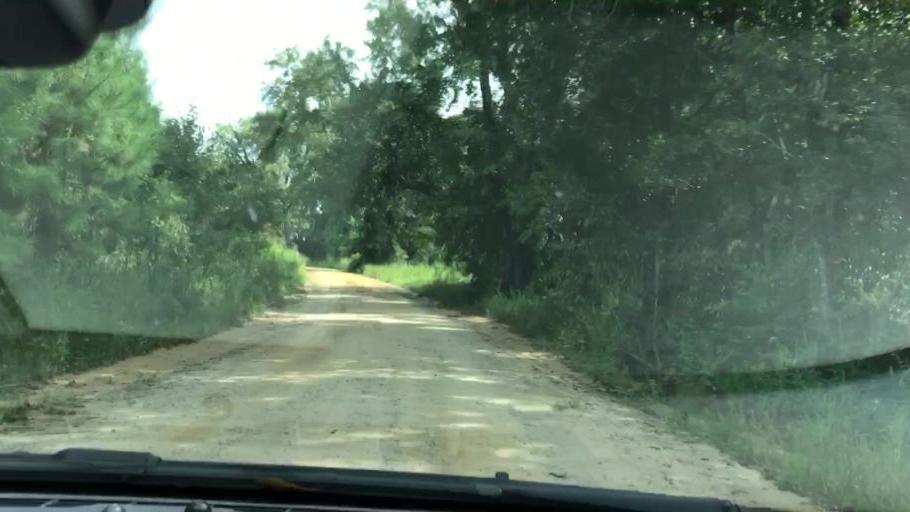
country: US
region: Georgia
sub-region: Clay County
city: Fort Gaines
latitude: 31.7234
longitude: -85.0749
